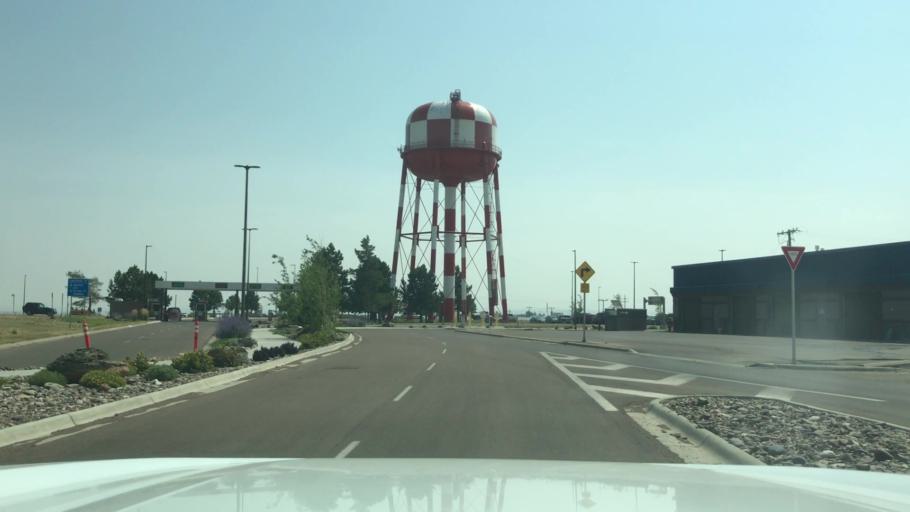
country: US
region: Montana
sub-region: Cascade County
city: Great Falls
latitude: 47.4805
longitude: -111.3585
